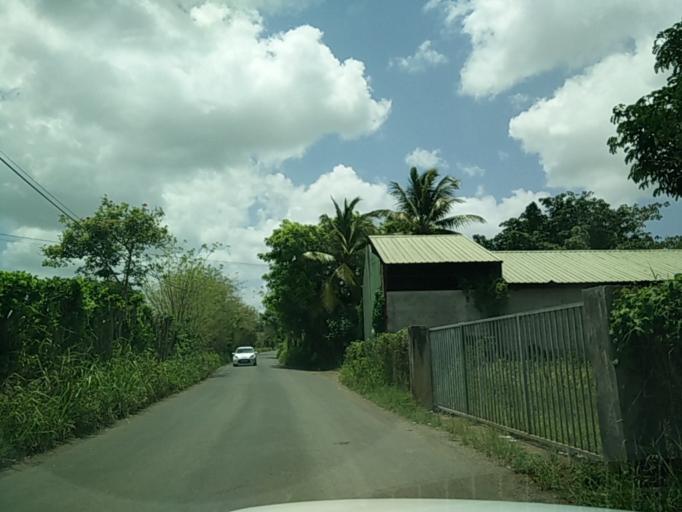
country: GP
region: Guadeloupe
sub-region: Guadeloupe
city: Les Abymes
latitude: 16.2807
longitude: -61.5169
